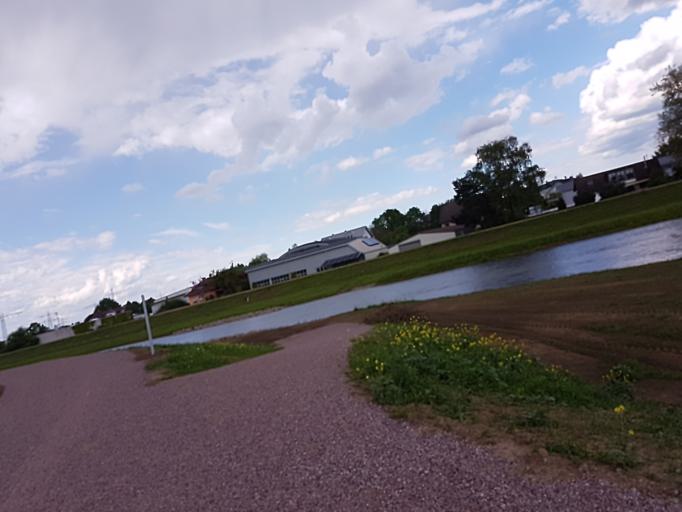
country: DE
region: Baden-Wuerttemberg
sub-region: Freiburg Region
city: Riegel
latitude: 48.1444
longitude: 7.7618
